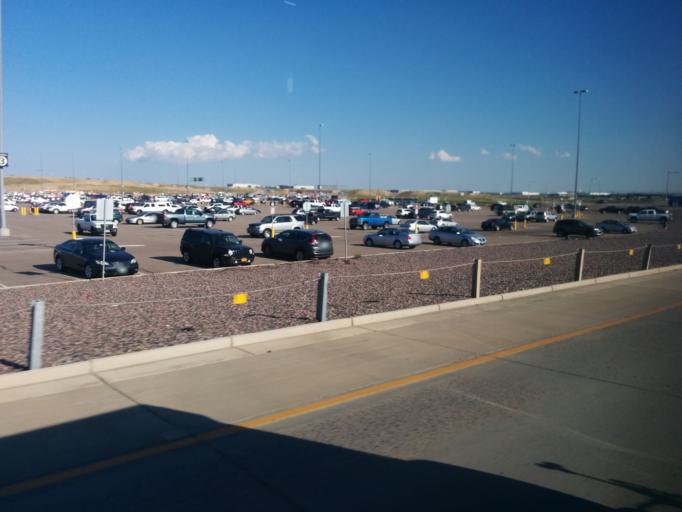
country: US
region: Colorado
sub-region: Weld County
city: Lochbuie
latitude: 39.8475
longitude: -104.6821
